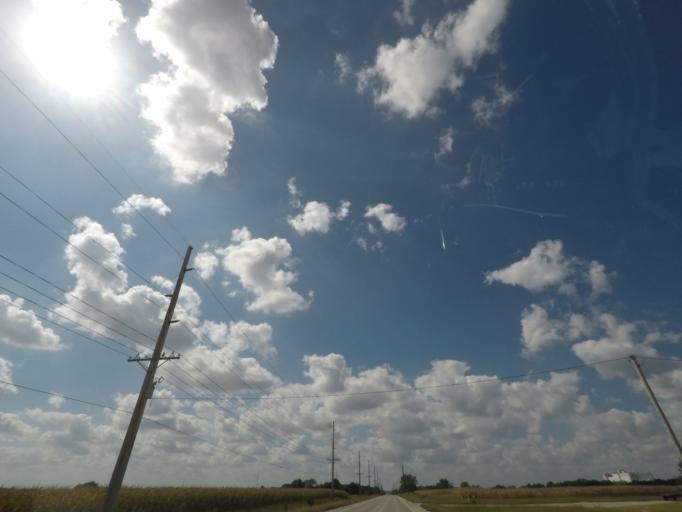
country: US
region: Iowa
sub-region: Story County
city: Ames
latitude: 42.0231
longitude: -93.5534
